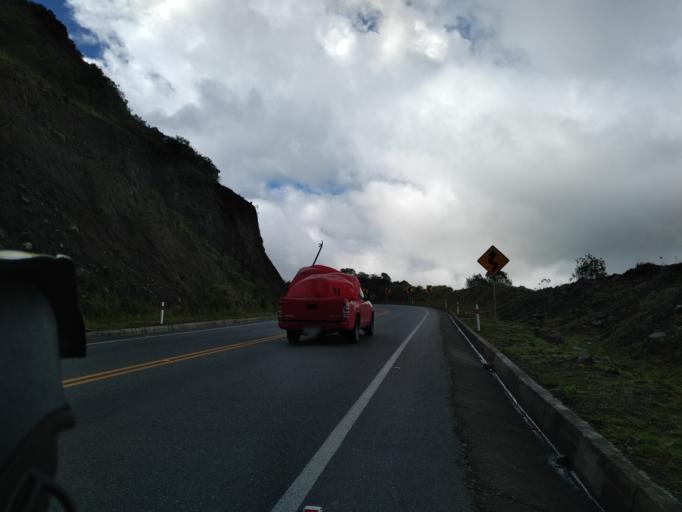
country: EC
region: Tungurahua
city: Banos
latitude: -1.4764
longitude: -78.5176
